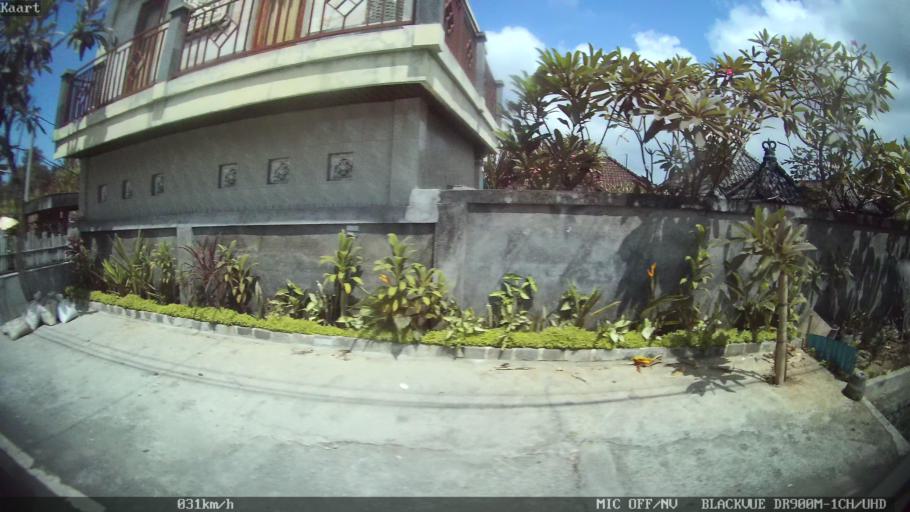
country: ID
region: Bali
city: Banjar Pasekan
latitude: -8.5996
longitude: 115.3010
